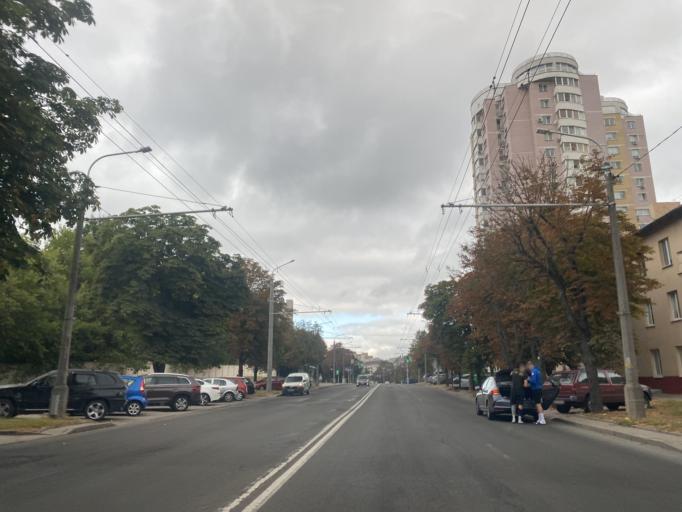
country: BY
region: Minsk
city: Minsk
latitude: 53.9225
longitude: 27.5618
